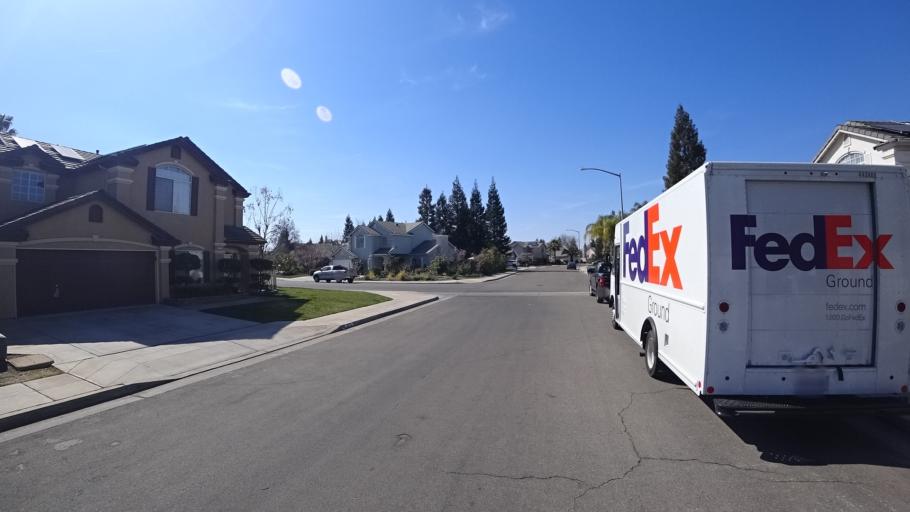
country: US
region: California
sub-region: Fresno County
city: Clovis
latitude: 36.8793
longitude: -119.7426
